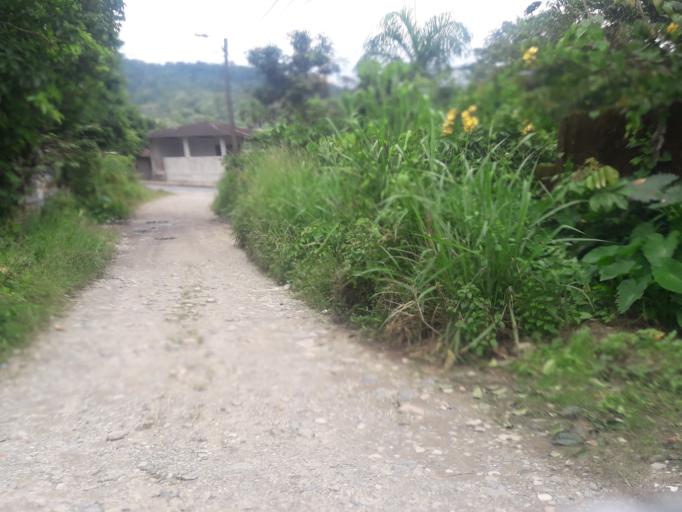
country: EC
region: Napo
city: Tena
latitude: -0.9774
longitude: -77.8533
